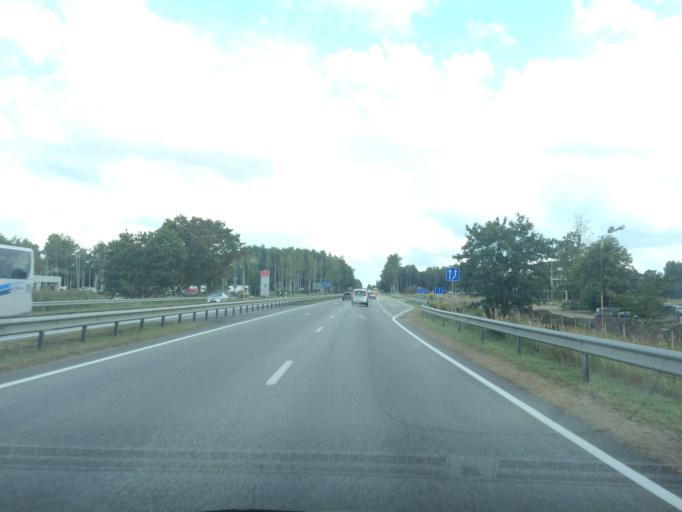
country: LV
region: Salaspils
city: Salaspils
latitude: 56.8564
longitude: 24.3200
